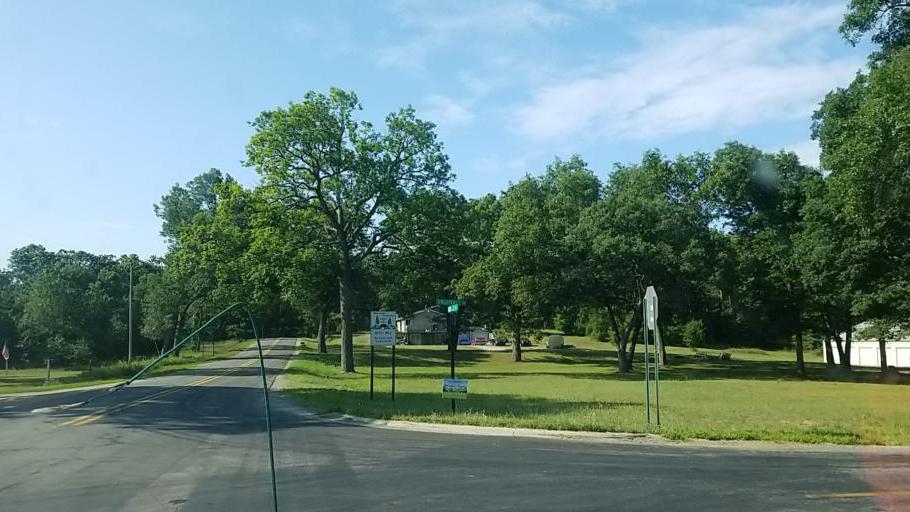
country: US
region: Michigan
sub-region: Muskegon County
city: Twin Lake
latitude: 43.4620
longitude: -86.1933
